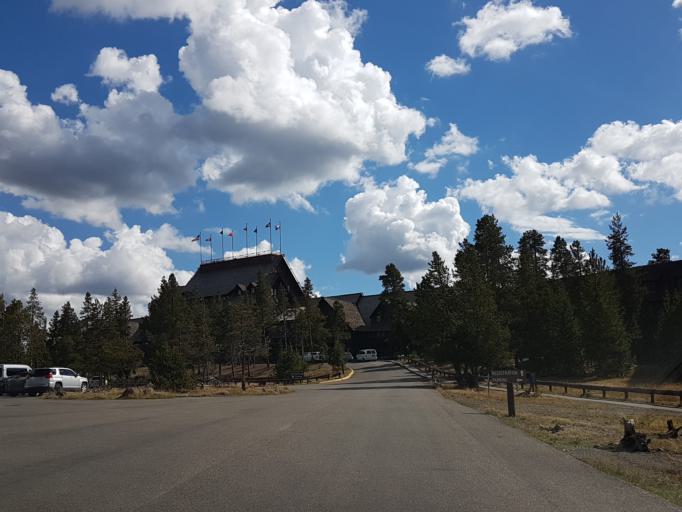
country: US
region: Montana
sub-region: Gallatin County
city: West Yellowstone
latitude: 44.4607
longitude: -110.8329
